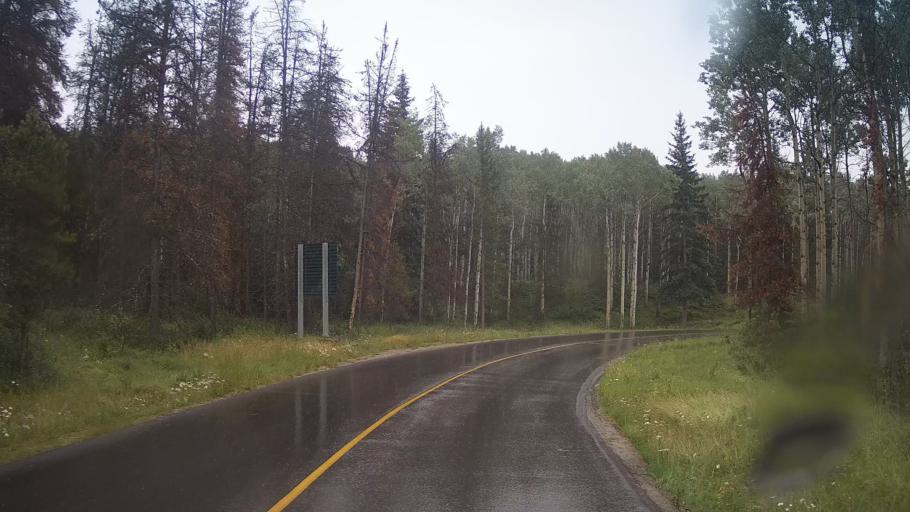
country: CA
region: Alberta
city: Jasper Park Lodge
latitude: 52.9128
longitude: -118.0928
